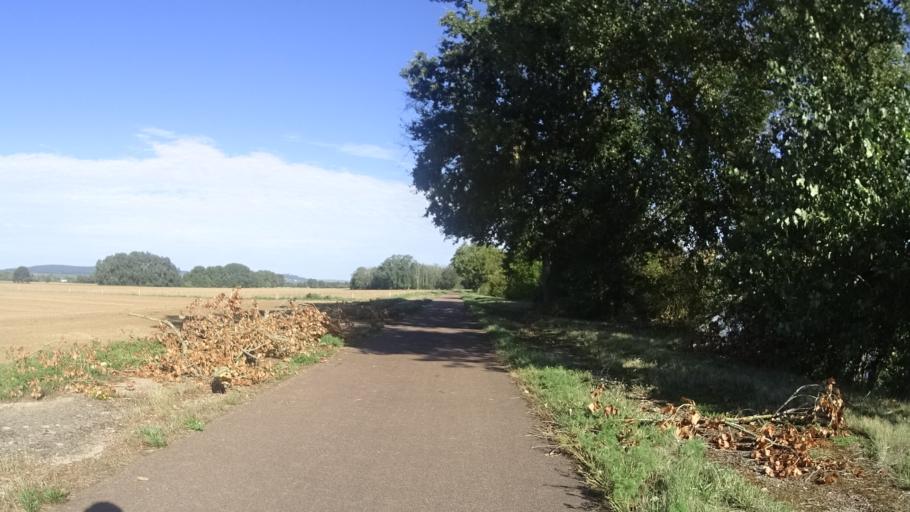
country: FR
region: Bourgogne
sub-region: Departement de la Nievre
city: Pouilly-sur-Loire
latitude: 47.2935
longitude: 2.9268
